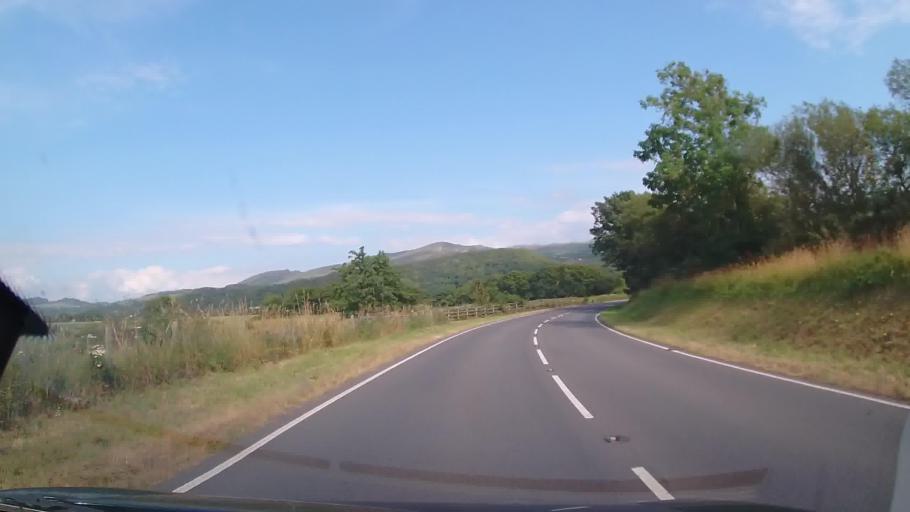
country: GB
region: Wales
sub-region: Gwynedd
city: Penrhyndeudraeth
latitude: 52.8971
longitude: -4.0841
